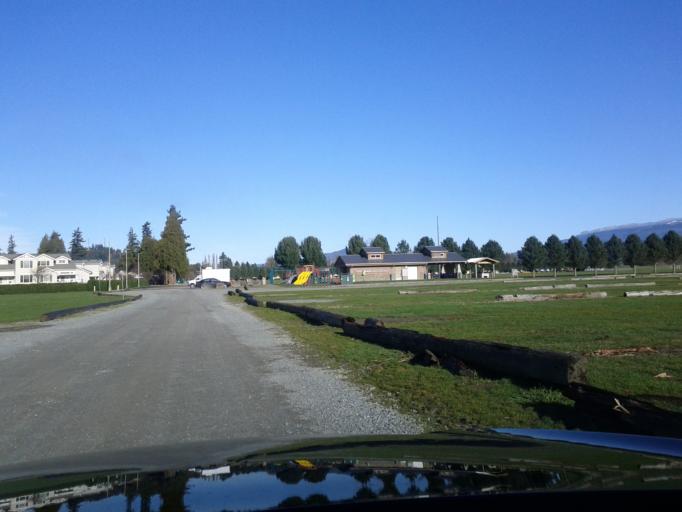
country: US
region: Washington
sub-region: Skagit County
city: Burlington
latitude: 48.4597
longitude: -122.3191
